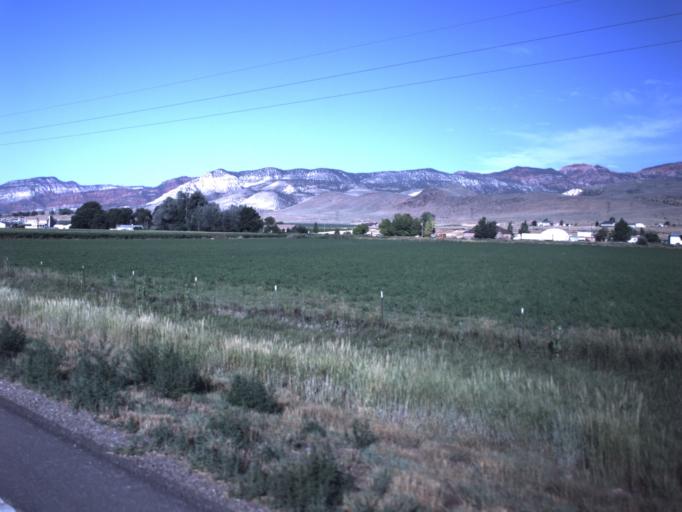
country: US
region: Utah
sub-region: Sevier County
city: Aurora
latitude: 38.9147
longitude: -111.9318
